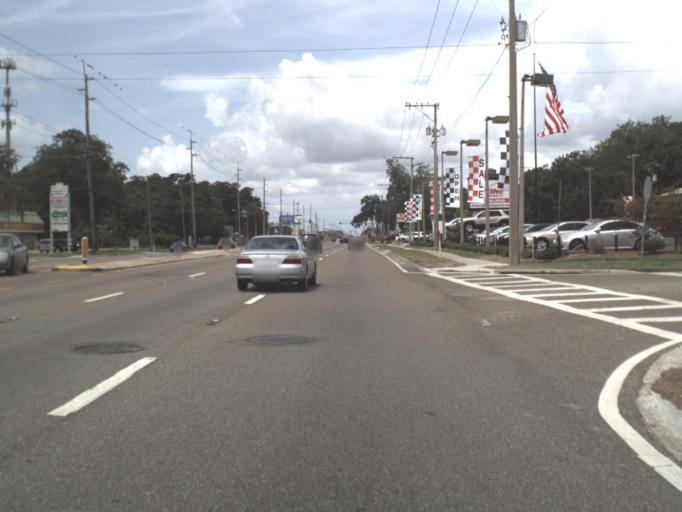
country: US
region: Florida
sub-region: Hillsborough County
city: Town 'n' Country
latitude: 27.9966
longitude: -82.5535
